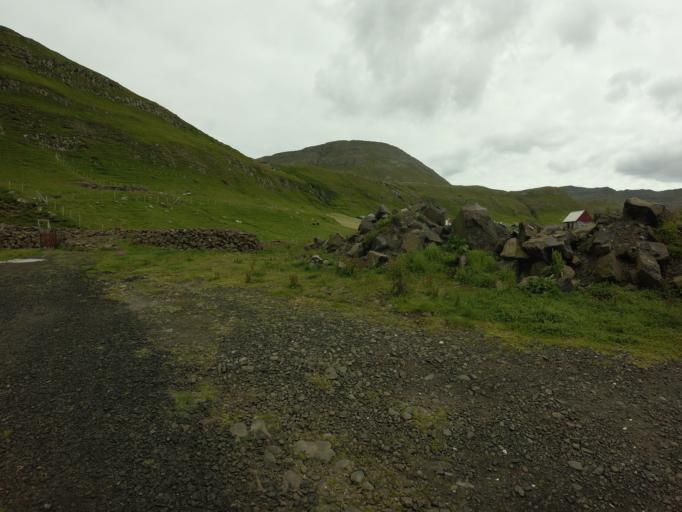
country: FO
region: Suduroy
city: Tvoroyri
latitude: 61.5266
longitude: -6.8853
